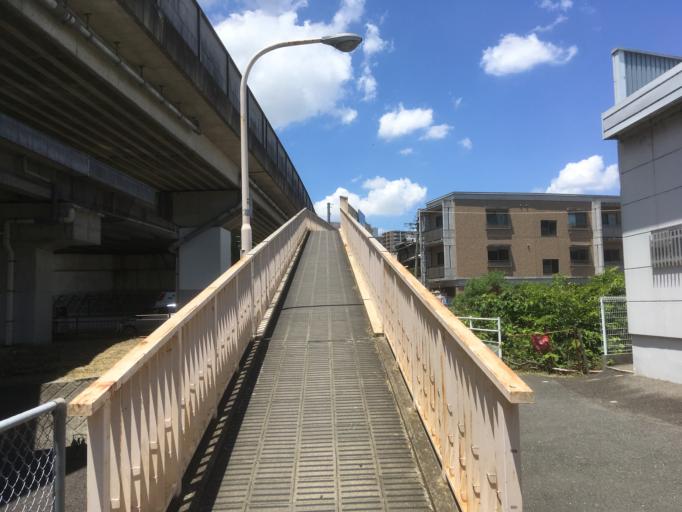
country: JP
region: Nara
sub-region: Ikoma-shi
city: Ikoma
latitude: 34.6934
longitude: 135.7029
